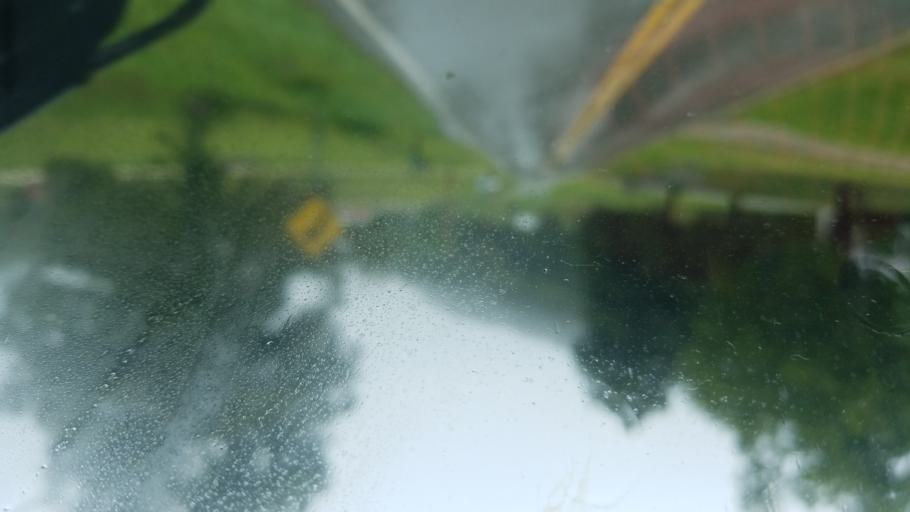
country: US
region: Kentucky
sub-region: Greenup County
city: South Shore
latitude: 38.6547
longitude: -82.9258
